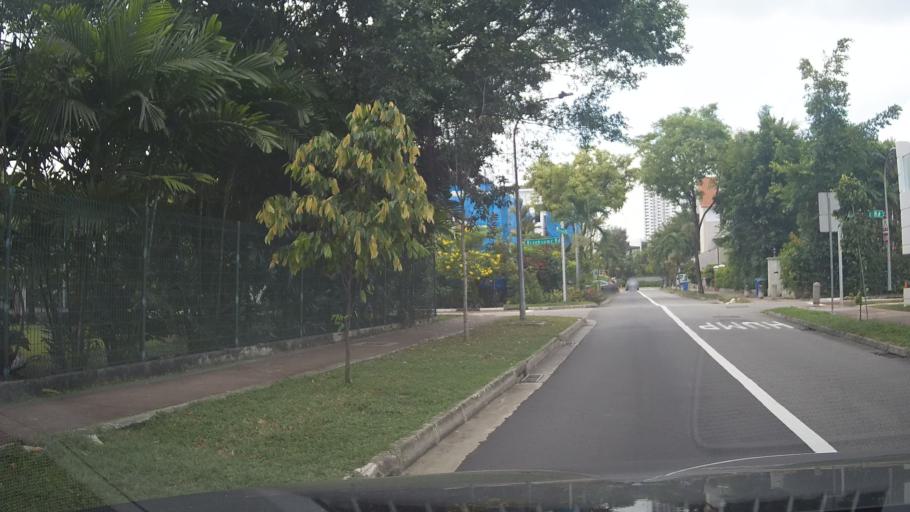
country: SG
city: Singapore
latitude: 1.3041
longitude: 103.8931
